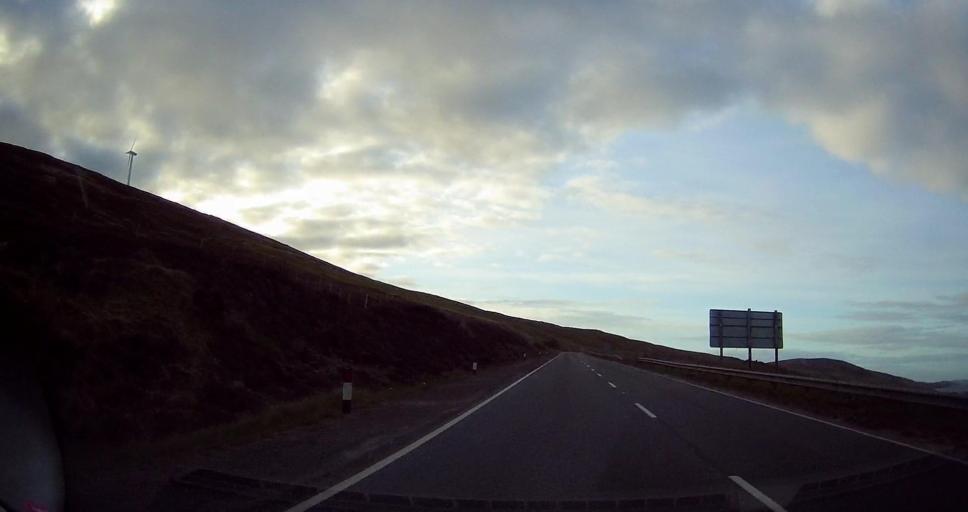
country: GB
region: Scotland
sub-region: Shetland Islands
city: Lerwick
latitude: 60.1616
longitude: -1.2267
